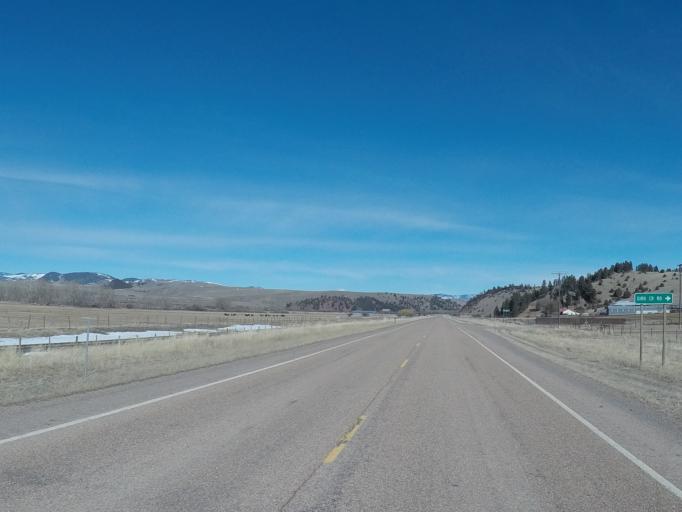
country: US
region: Montana
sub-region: Granite County
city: Philipsburg
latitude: 46.4969
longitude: -113.2223
